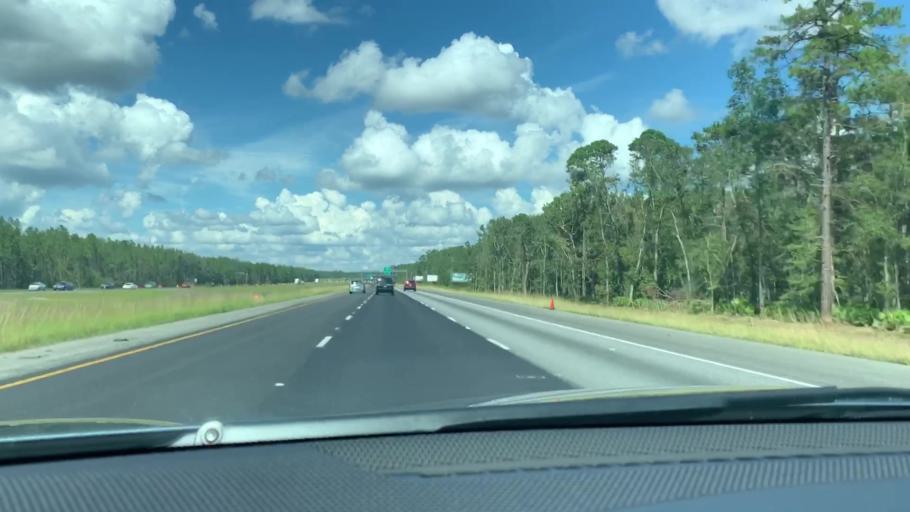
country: US
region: Georgia
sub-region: Camden County
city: Woodbine
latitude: 30.9301
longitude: -81.6858
